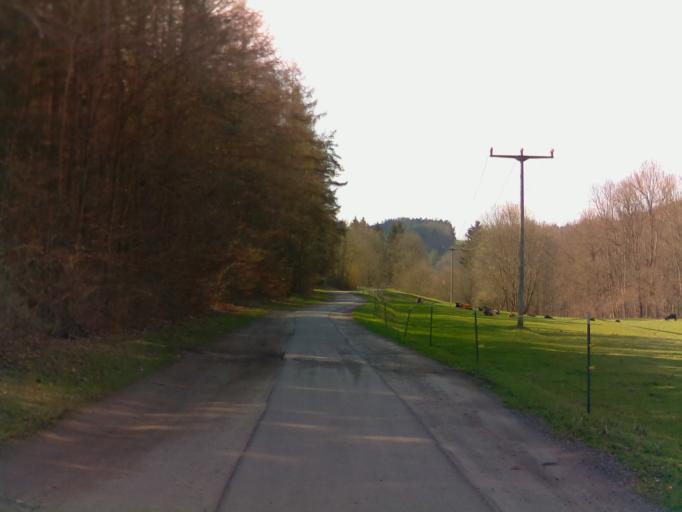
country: DE
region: Thuringia
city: Altenberga
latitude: 50.8307
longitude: 11.5132
